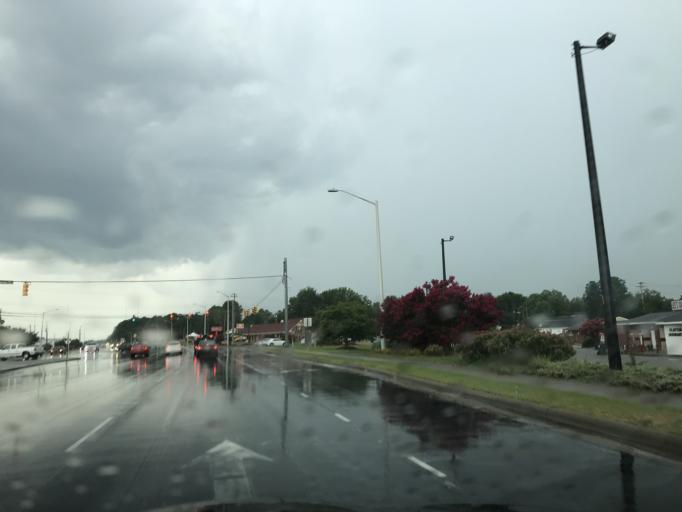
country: US
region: North Carolina
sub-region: Johnston County
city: Clayton
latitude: 35.6417
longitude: -78.4504
